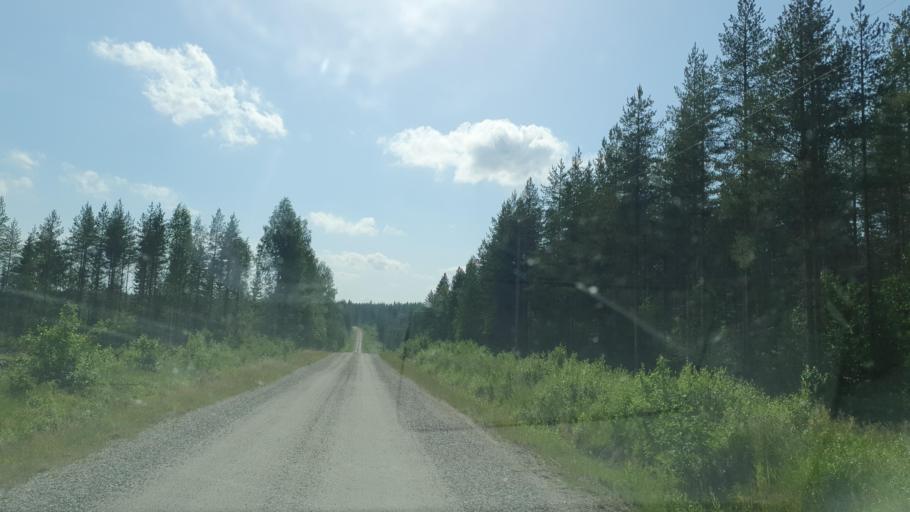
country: FI
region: Kainuu
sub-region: Kehys-Kainuu
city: Kuhmo
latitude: 64.0367
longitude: 29.9414
